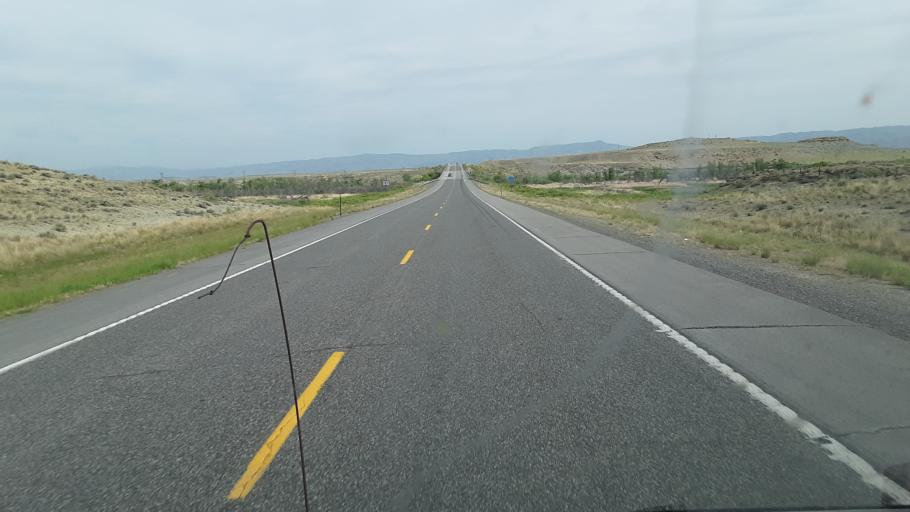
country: US
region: Wyoming
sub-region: Fremont County
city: Riverton
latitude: 43.2708
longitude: -108.1155
